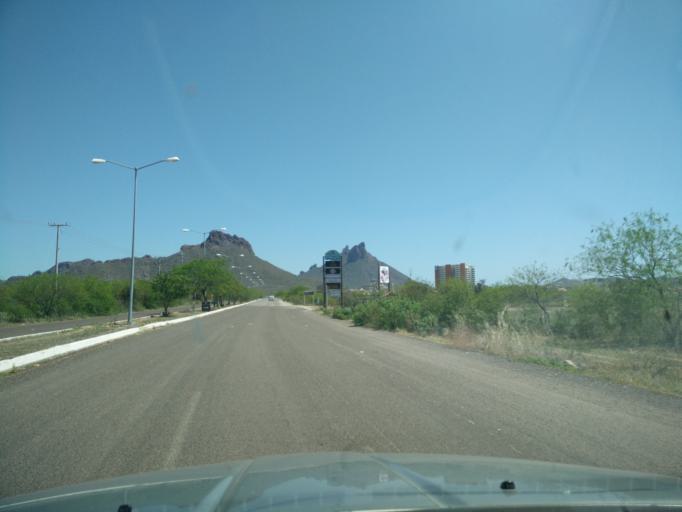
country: MX
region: Sonora
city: Heroica Guaymas
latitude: 27.9729
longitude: -111.1109
